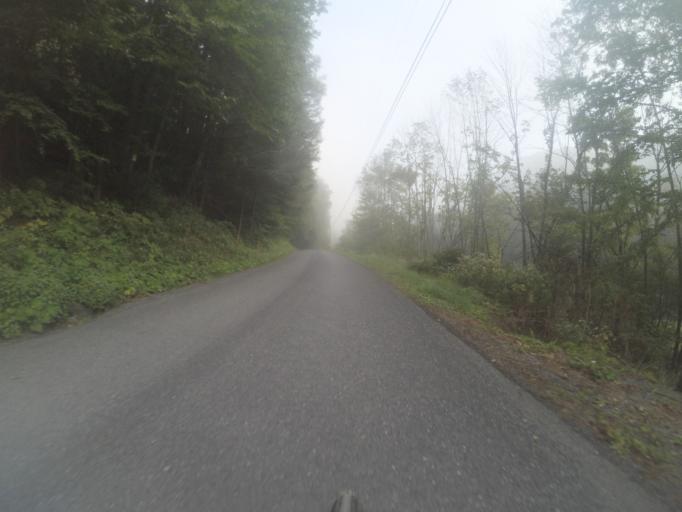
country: US
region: Pennsylvania
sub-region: Mifflin County
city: Milroy
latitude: 40.8553
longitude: -77.4594
